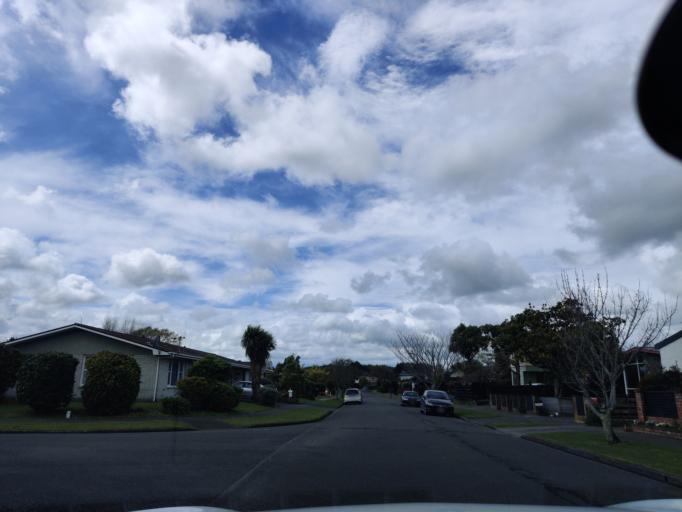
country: NZ
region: Manawatu-Wanganui
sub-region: Palmerston North City
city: Palmerston North
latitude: -40.3805
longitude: 175.5950
